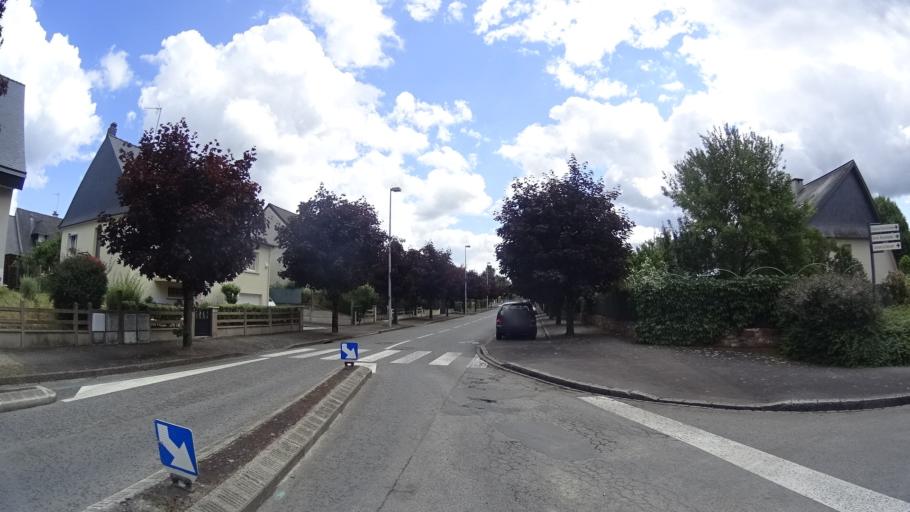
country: FR
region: Brittany
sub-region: Departement d'Ille-et-Vilaine
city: Chartres-de-Bretagne
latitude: 48.0387
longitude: -1.7022
